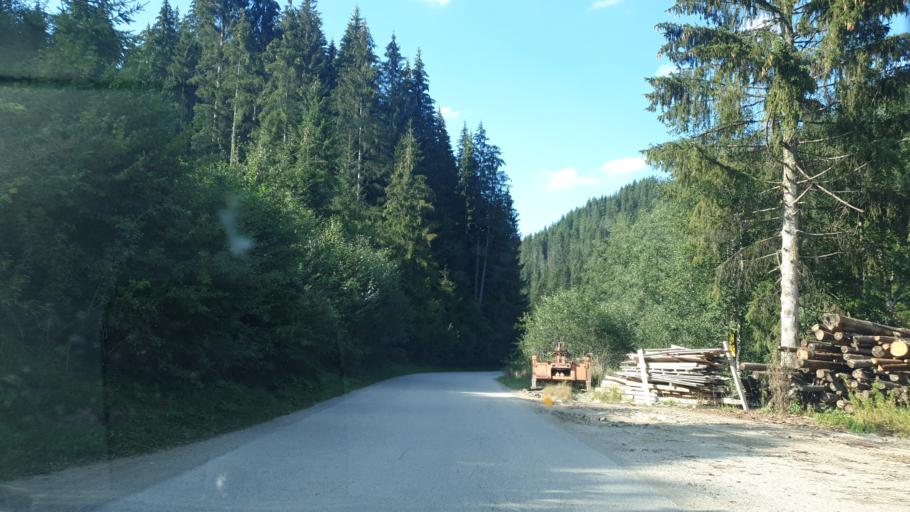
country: RS
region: Central Serbia
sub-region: Zlatiborski Okrug
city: Nova Varos
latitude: 43.4525
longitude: 19.8428
